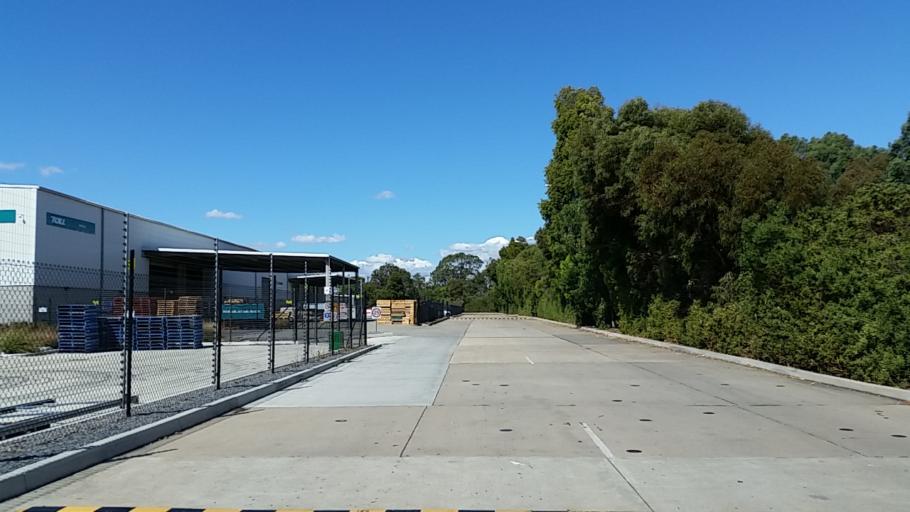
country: AU
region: South Australia
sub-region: Charles Sturt
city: Woodville North
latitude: -34.8758
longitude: 138.5330
